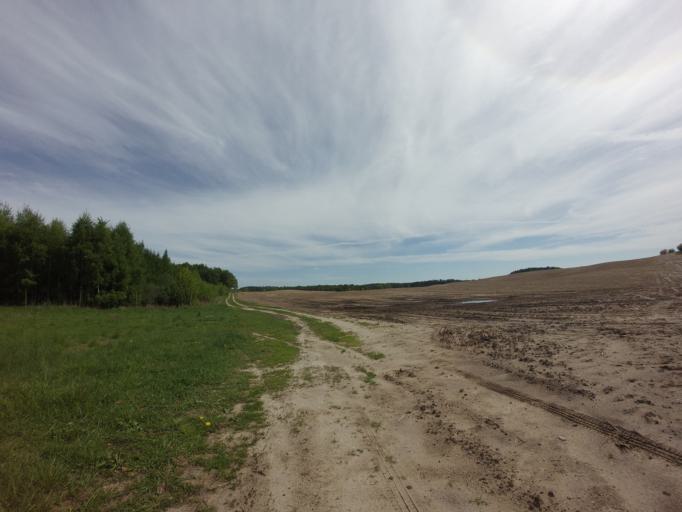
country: PL
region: West Pomeranian Voivodeship
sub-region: Powiat choszczenski
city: Recz
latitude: 53.1588
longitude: 15.5744
